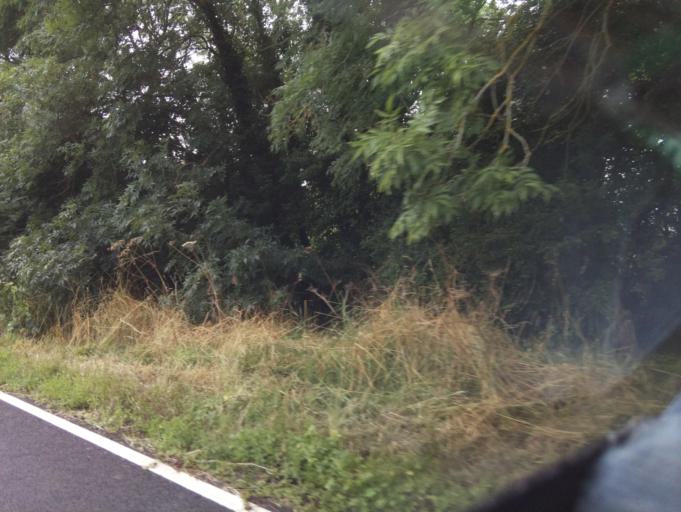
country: GB
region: England
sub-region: District of Rutland
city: Ryhall
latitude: 52.6861
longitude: -0.4739
